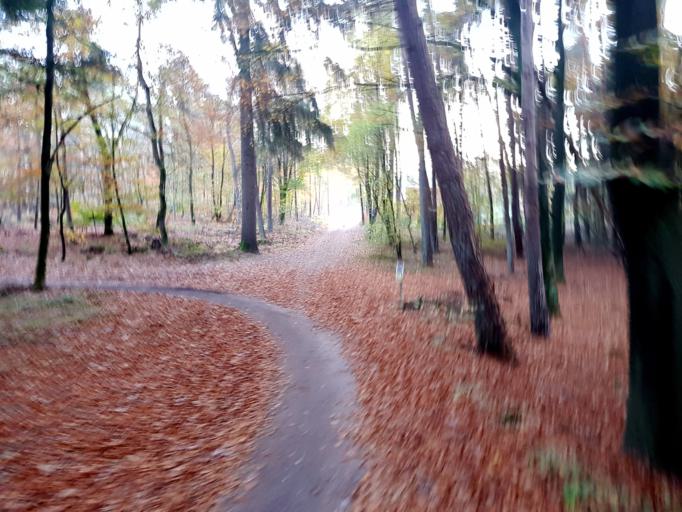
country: NL
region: Gelderland
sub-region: Gemeente Groesbeek
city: Berg en Dal
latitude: 51.7853
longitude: 5.8940
